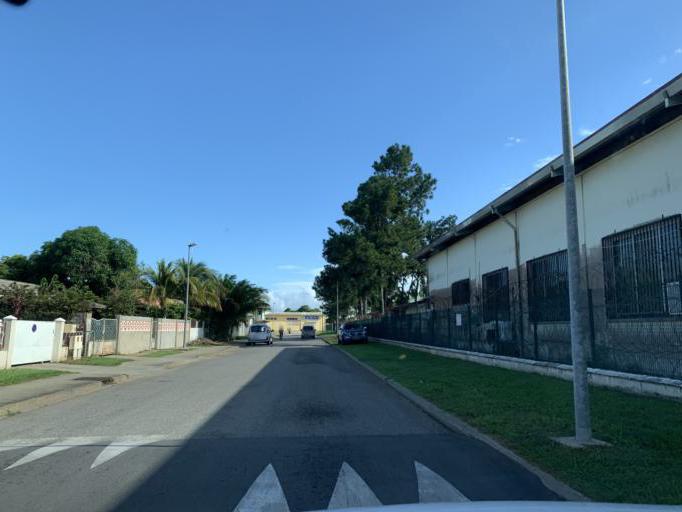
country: GF
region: Guyane
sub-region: Guyane
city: Kourou
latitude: 5.1710
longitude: -52.6452
